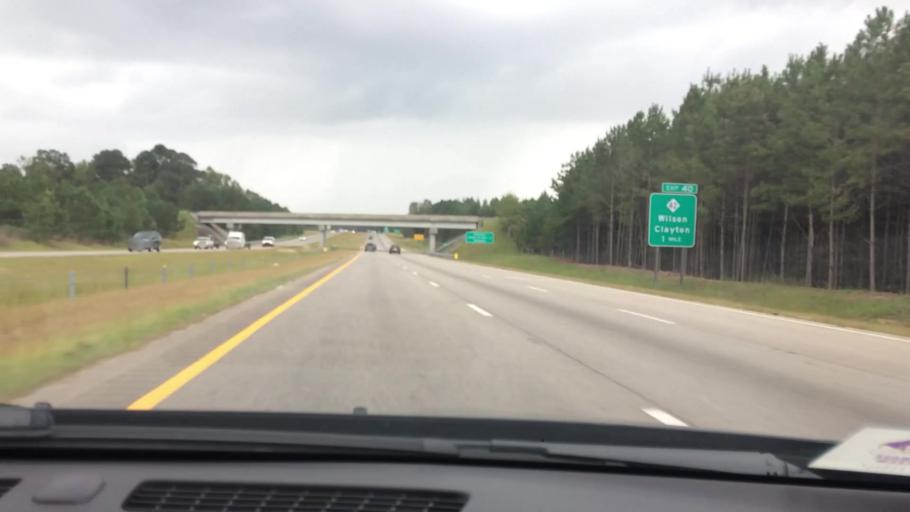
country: US
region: North Carolina
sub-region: Wilson County
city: Lucama
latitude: 35.7288
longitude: -78.0088
